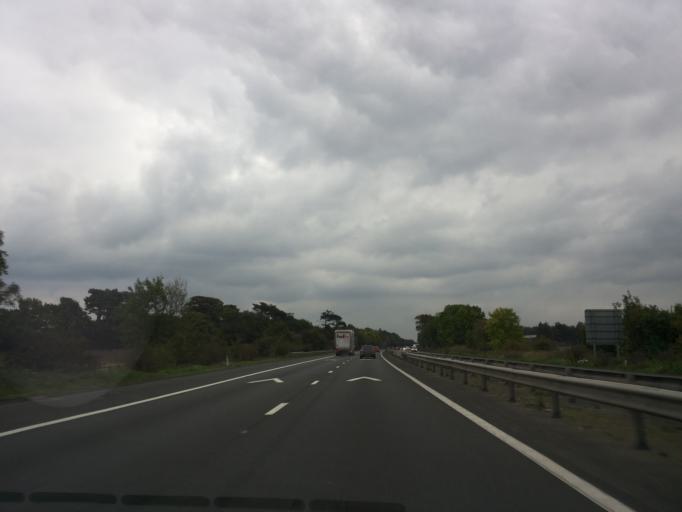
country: GB
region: England
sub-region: Kent
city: Teynham
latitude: 51.2974
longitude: 0.7807
